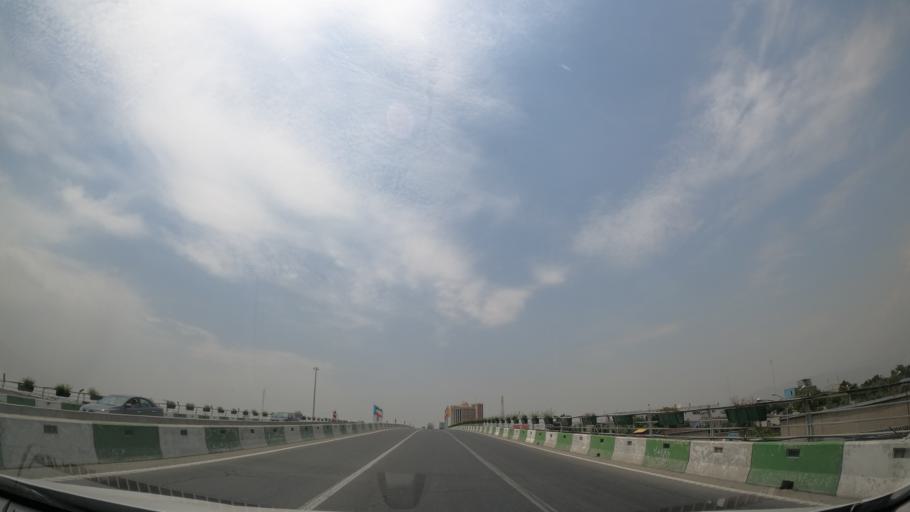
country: IR
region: Tehran
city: Tehran
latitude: 35.6757
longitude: 51.3107
